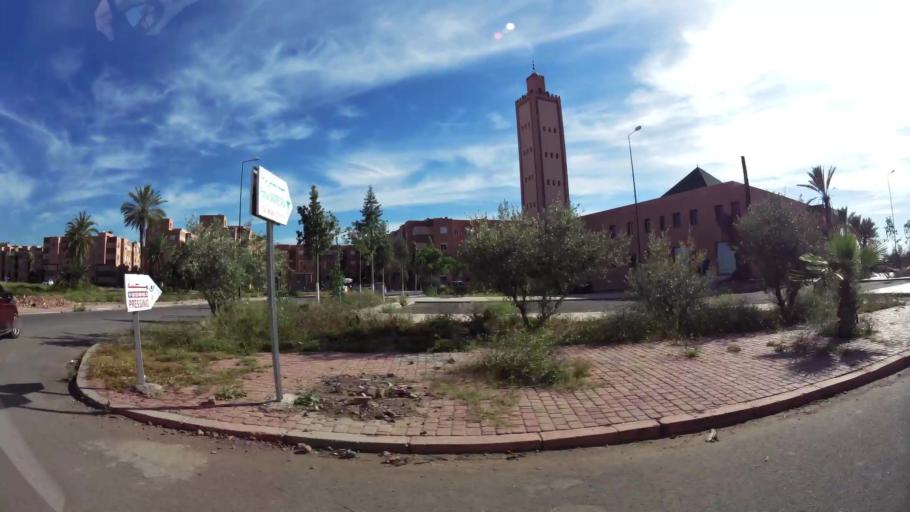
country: MA
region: Marrakech-Tensift-Al Haouz
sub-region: Marrakech
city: Marrakesh
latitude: 31.6746
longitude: -8.0553
